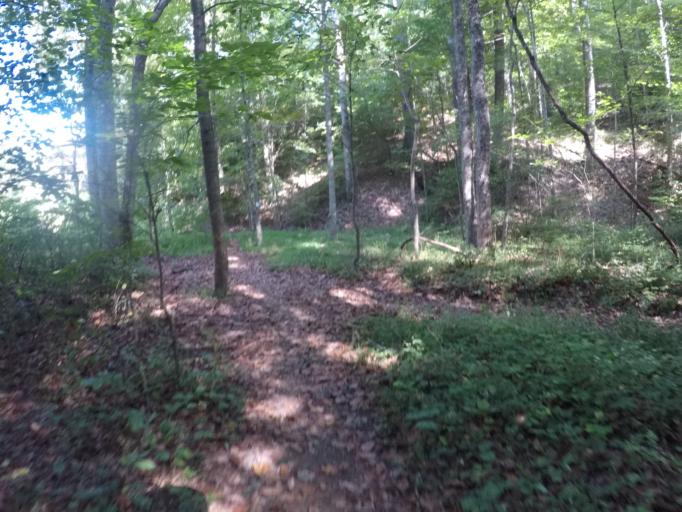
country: US
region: Ohio
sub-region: Lawrence County
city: Ironton
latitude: 38.6192
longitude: -82.6218
